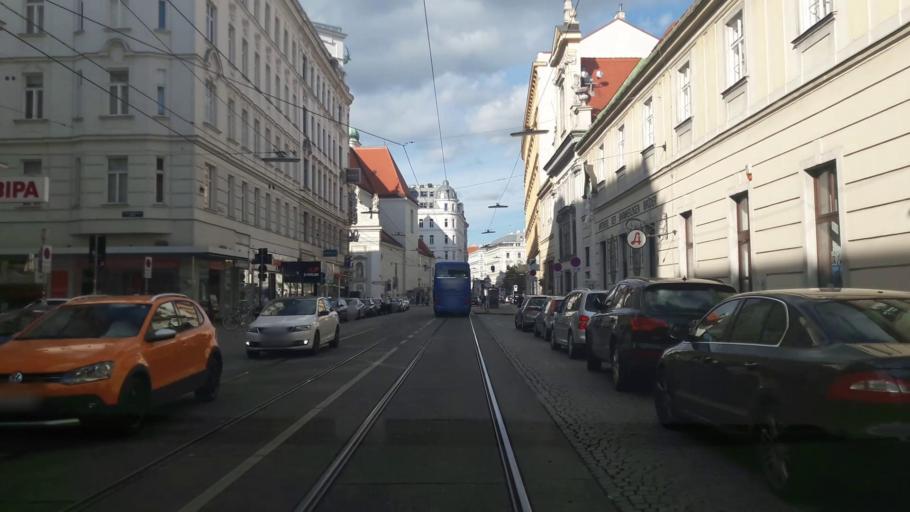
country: AT
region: Vienna
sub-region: Wien Stadt
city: Vienna
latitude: 48.2148
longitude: 16.3800
